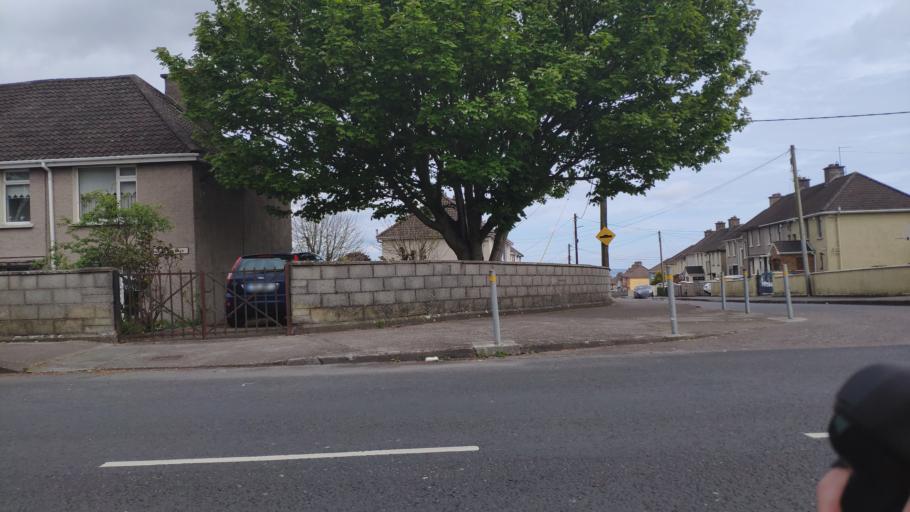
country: IE
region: Munster
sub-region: County Cork
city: Cork
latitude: 51.9057
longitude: -8.4963
